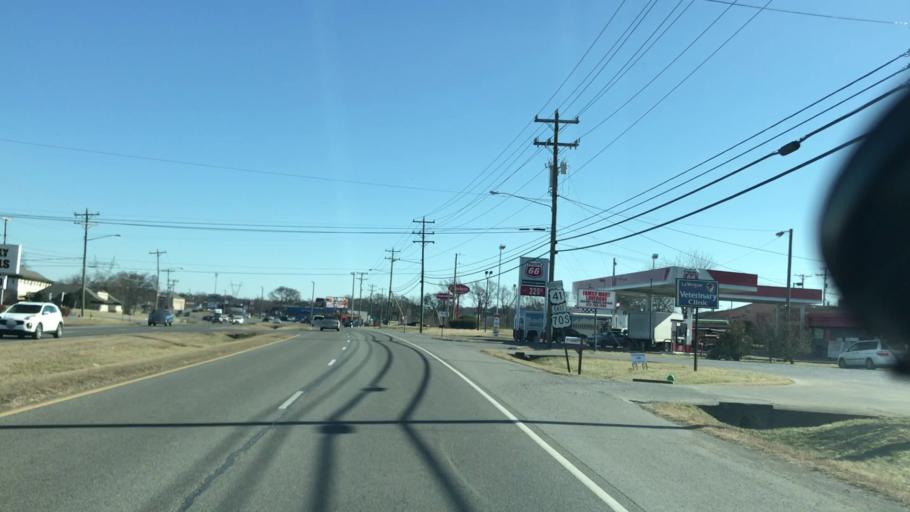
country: US
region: Tennessee
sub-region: Rutherford County
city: La Vergne
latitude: 36.0234
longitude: -86.5850
